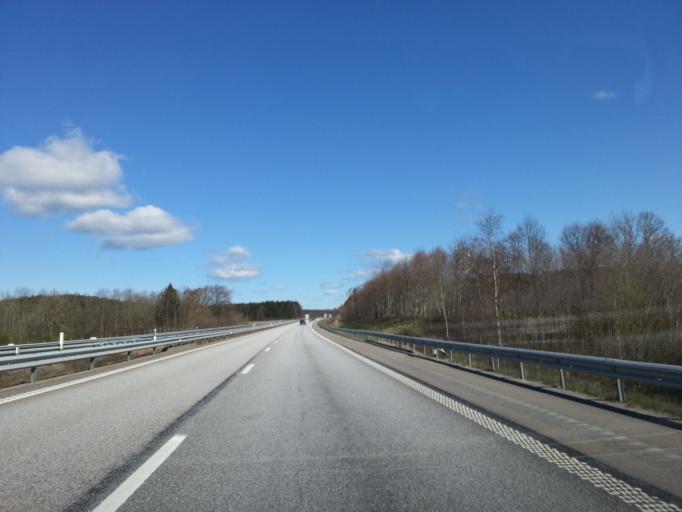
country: SE
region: Vaestra Goetaland
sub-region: Uddevalla Kommun
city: Uddevalla
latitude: 58.3043
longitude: 11.8597
